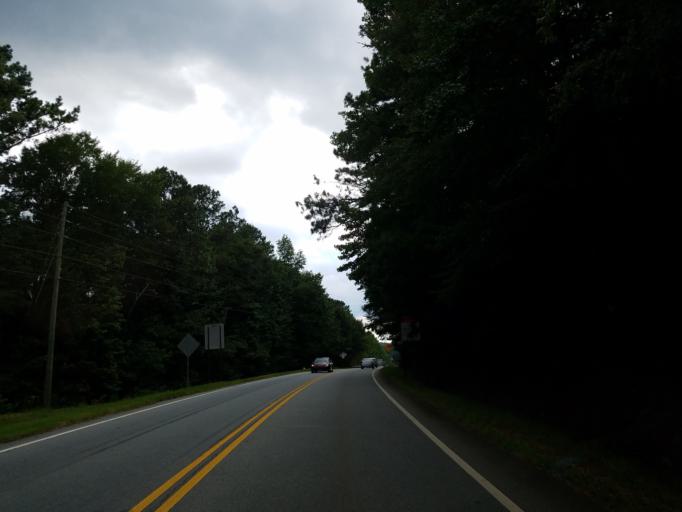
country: US
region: Georgia
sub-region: Floyd County
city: Shannon
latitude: 34.3680
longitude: -85.0582
